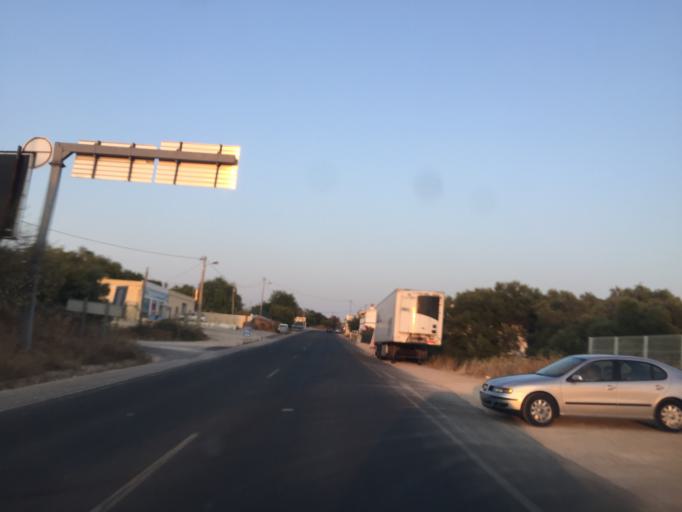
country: PT
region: Faro
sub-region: Loule
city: Almancil
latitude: 37.0811
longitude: -8.0062
